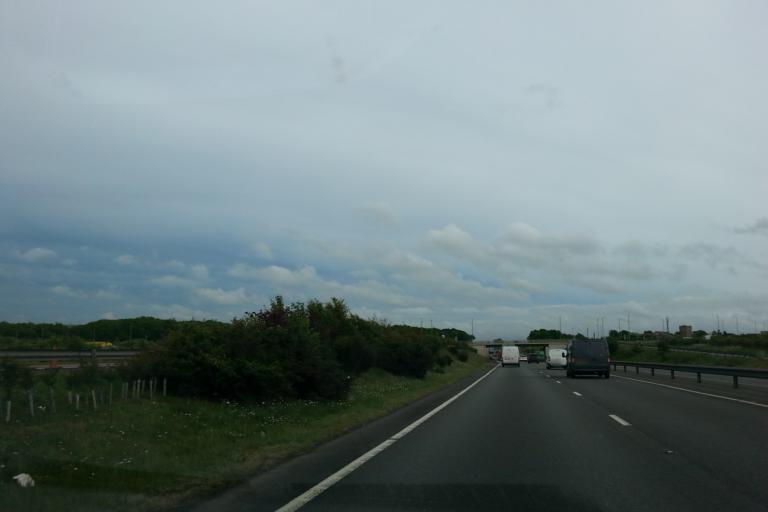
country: GB
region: England
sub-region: Nottinghamshire
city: Bircotes
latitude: 53.3901
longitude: -1.0673
